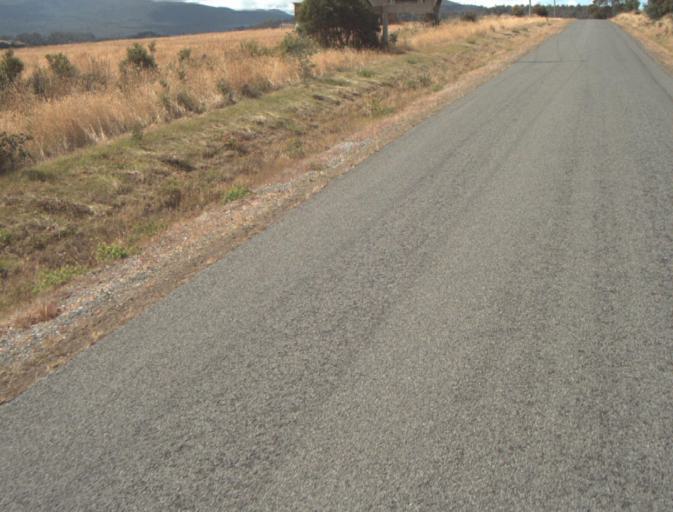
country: AU
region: Tasmania
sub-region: Launceston
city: Mayfield
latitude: -41.2318
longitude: 147.1461
